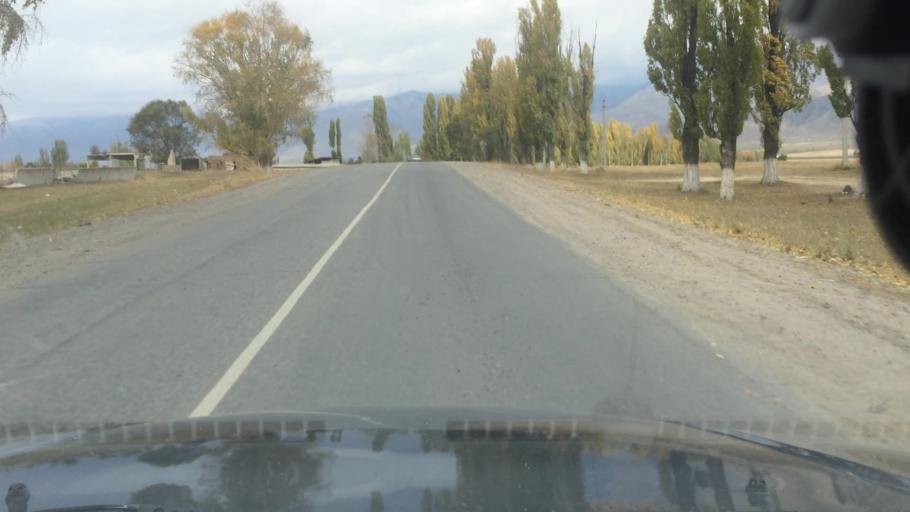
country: KG
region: Ysyk-Koel
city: Tyup
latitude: 42.7415
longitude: 78.3416
